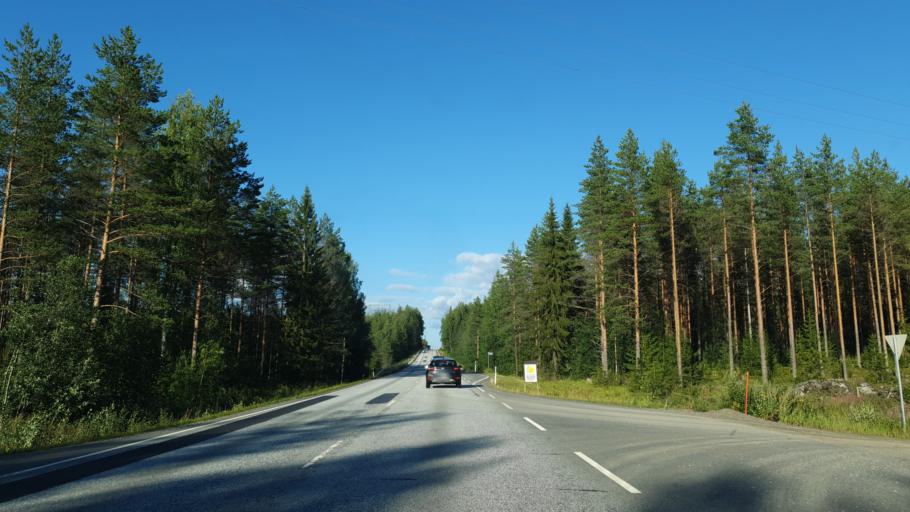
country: FI
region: North Karelia
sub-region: Joensuu
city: Outokumpu
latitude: 62.5248
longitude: 29.0610
